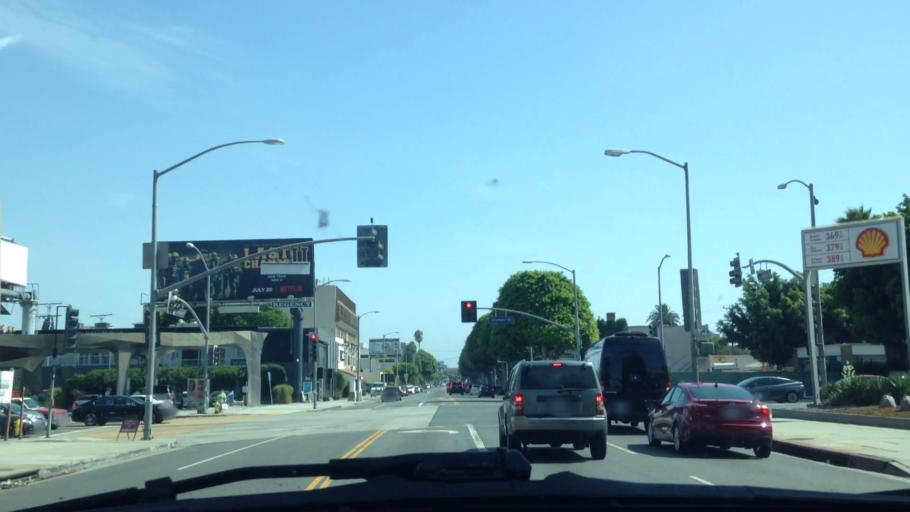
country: US
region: California
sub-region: Los Angeles County
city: Beverly Hills
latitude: 34.0598
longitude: -118.3836
